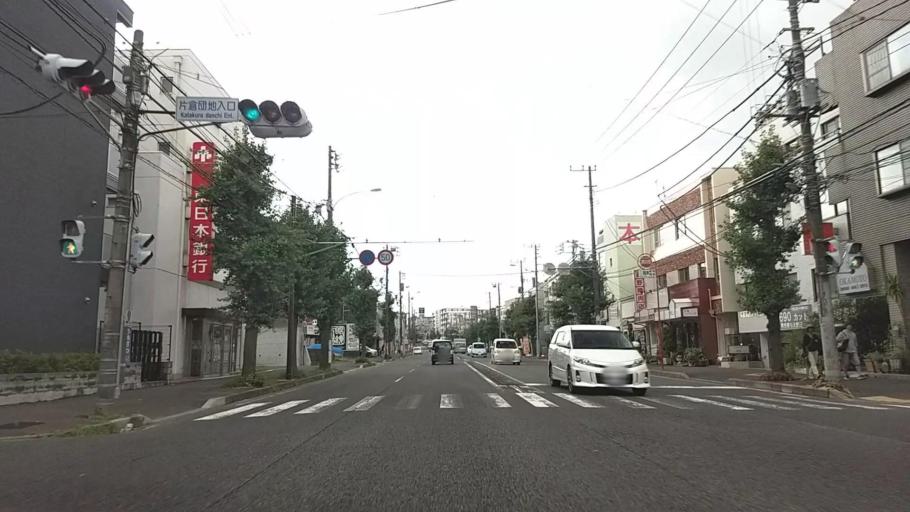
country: JP
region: Kanagawa
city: Yokohama
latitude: 35.4864
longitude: 139.6039
